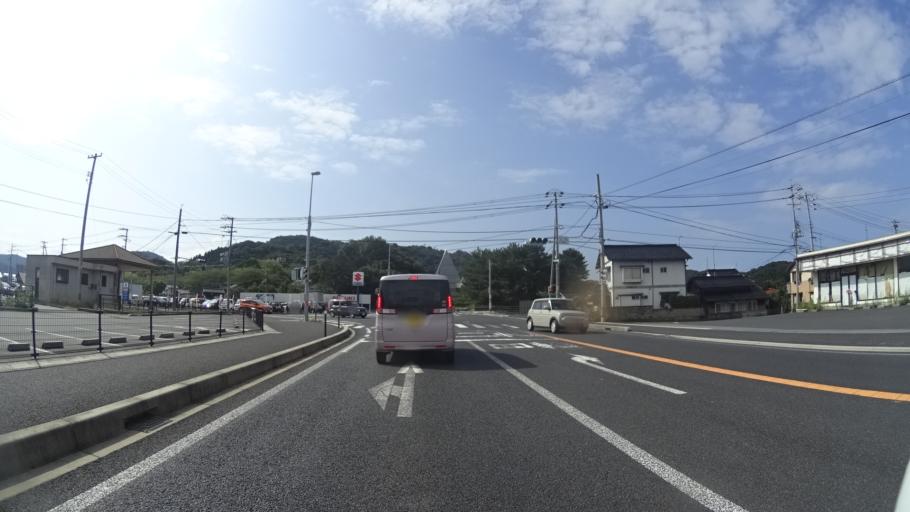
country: JP
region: Shimane
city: Odacho-oda
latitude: 35.1486
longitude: 132.4050
